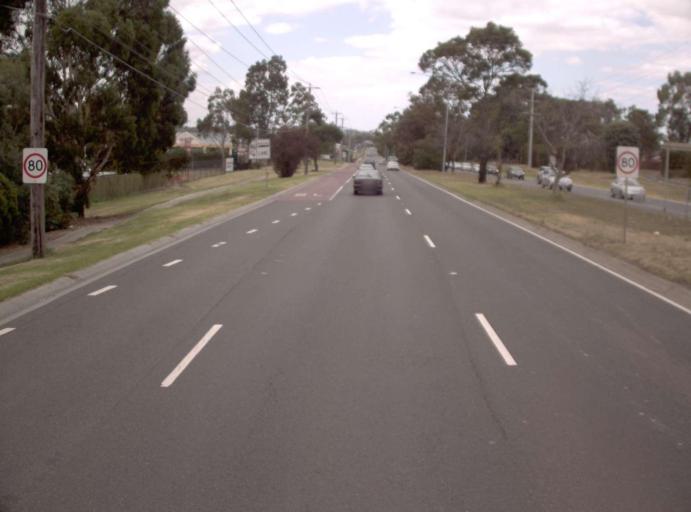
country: AU
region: Victoria
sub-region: Knox
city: Rowville
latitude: -37.9170
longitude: 145.2351
